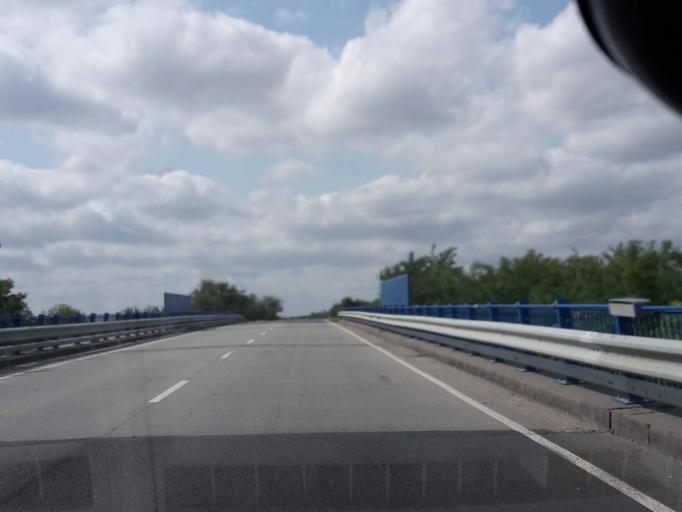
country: CZ
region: South Moravian
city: Vinicne Sumice
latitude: 49.1910
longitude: 16.8493
